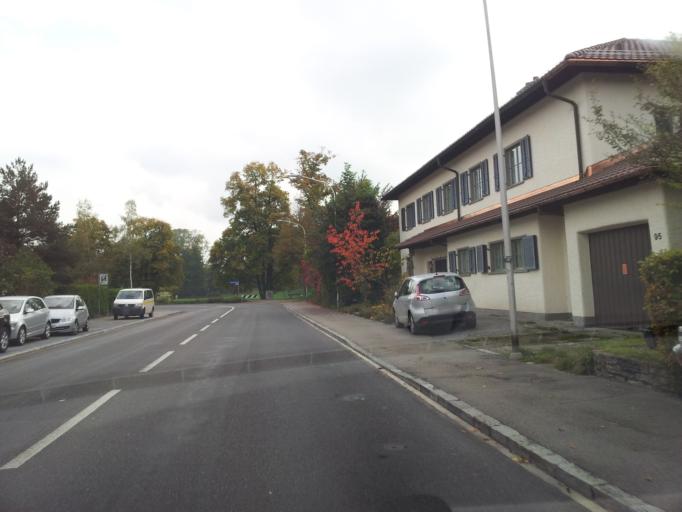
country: CH
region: Bern
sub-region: Bern-Mittelland District
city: Muri
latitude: 46.9341
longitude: 7.4680
